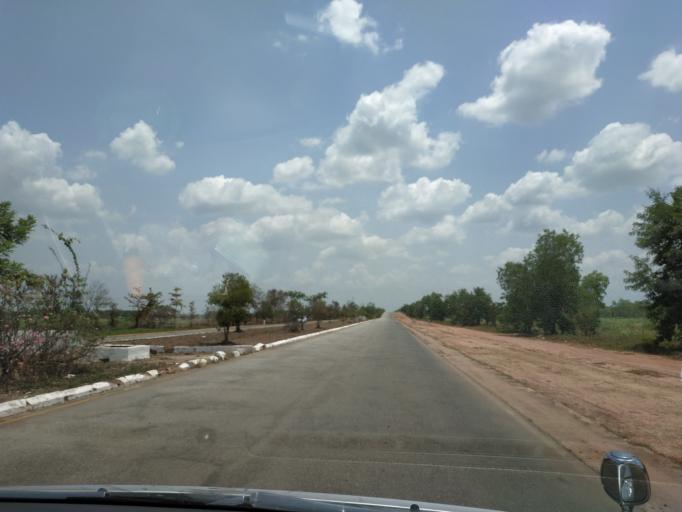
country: MM
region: Bago
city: Thanatpin
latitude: 17.2469
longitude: 96.2301
